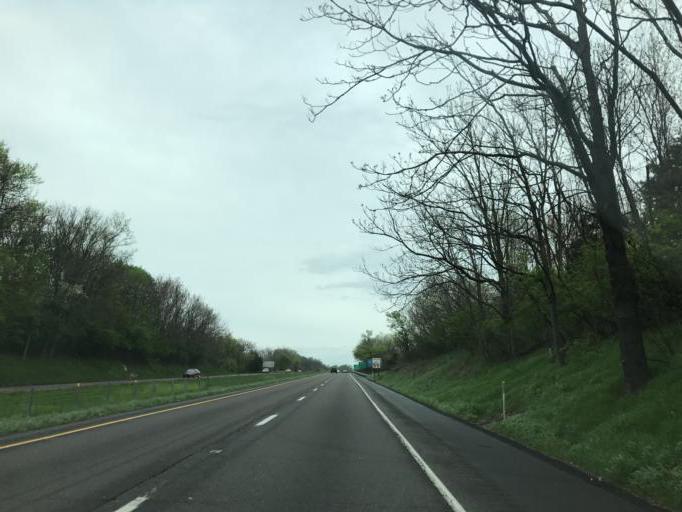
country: US
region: Pennsylvania
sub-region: Berks County
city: Spring Ridge
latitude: 40.3704
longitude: -75.9898
